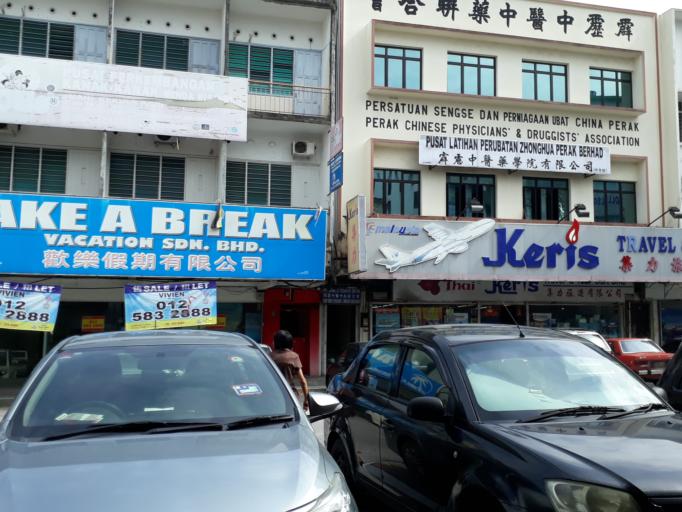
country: MY
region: Perak
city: Ipoh
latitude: 4.5913
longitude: 101.0857
